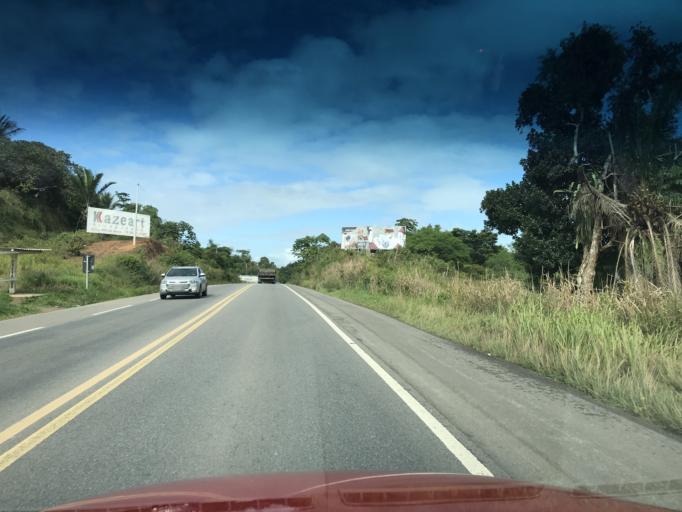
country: BR
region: Bahia
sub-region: Conceicao Do Almeida
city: Muritiba
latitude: -12.9195
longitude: -39.2466
